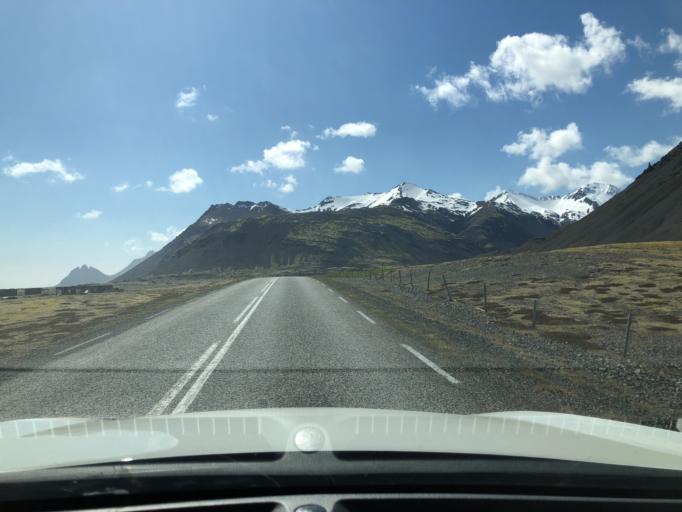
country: IS
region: East
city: Hoefn
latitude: 64.3951
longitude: -14.9219
